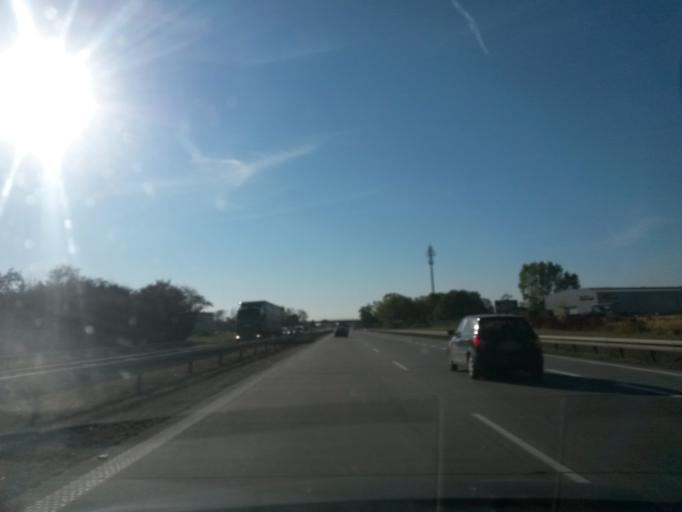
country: PL
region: Lower Silesian Voivodeship
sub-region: Powiat wroclawski
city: Tyniec Maly
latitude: 51.0385
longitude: 16.8989
